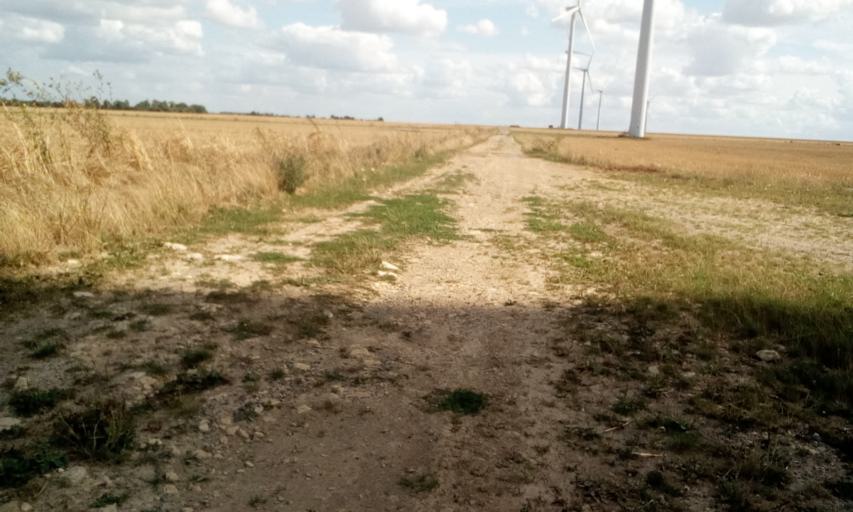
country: FR
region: Lower Normandy
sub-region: Departement du Calvados
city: Bellengreville
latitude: 49.1058
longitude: -0.2386
